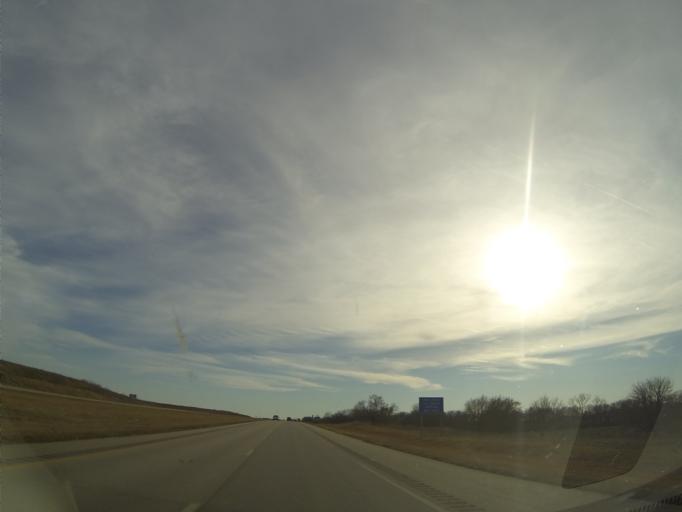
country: US
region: Kansas
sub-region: Ottawa County
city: Minneapolis
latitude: 39.1307
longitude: -97.6693
